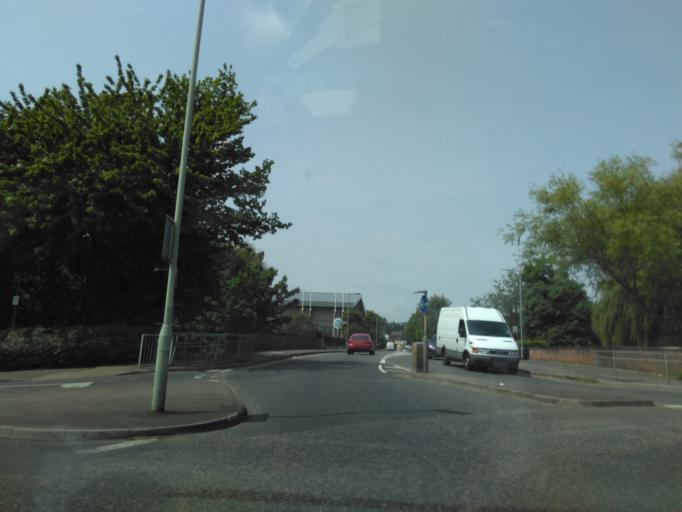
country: GB
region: England
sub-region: Kent
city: Canterbury
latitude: 51.2855
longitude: 1.0850
